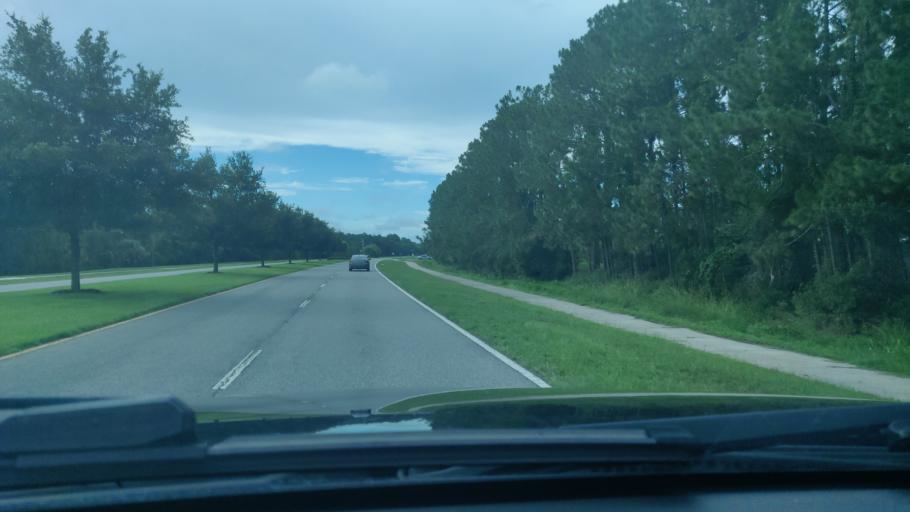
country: US
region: Florida
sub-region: Flagler County
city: Bunnell
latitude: 29.5219
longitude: -81.2252
